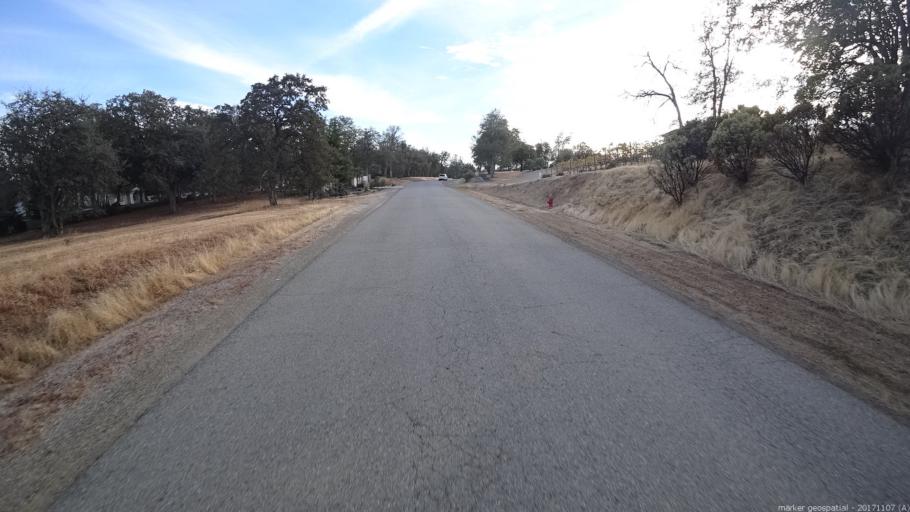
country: US
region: California
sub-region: Shasta County
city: Shasta
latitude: 40.5118
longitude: -122.4737
